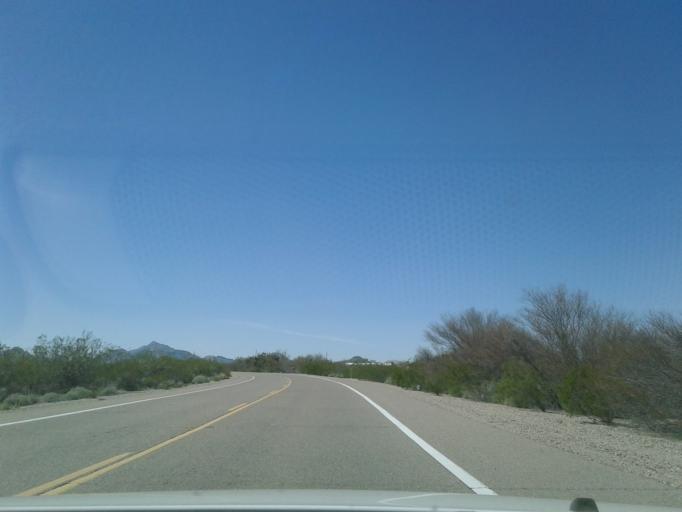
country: US
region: Arizona
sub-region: Pima County
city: Avra Valley
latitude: 32.3787
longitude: -111.3489
